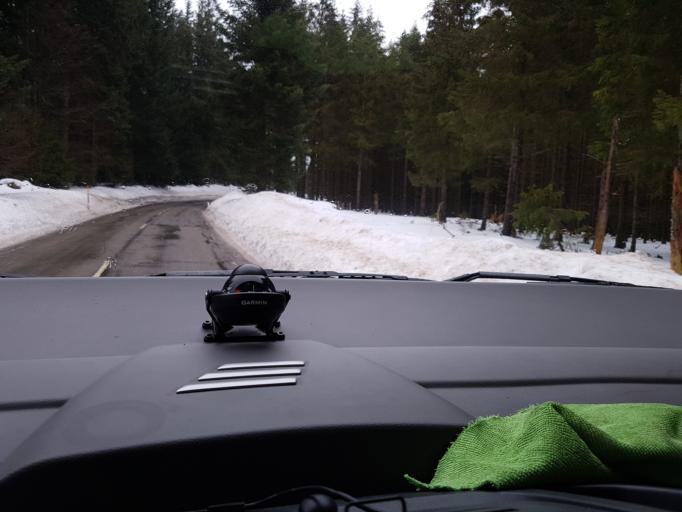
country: FR
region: Lorraine
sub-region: Departement des Vosges
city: Plainfaing
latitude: 48.1537
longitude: 7.0715
